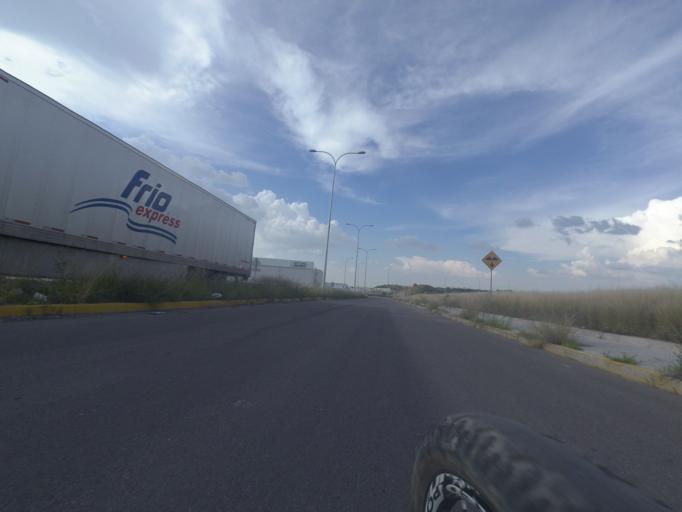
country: MX
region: Aguascalientes
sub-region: Aguascalientes
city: Penuelas (El Cienegal)
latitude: 21.7259
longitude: -102.2881
